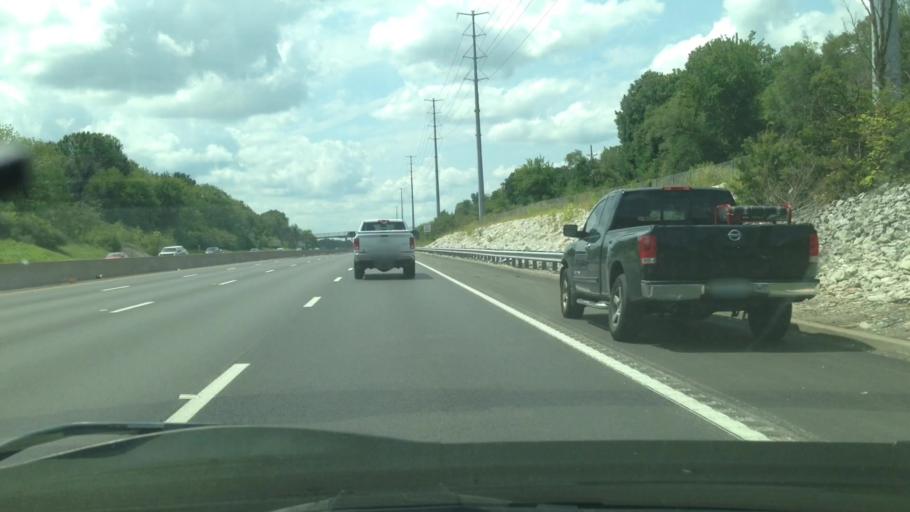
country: US
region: Missouri
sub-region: Saint Louis County
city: Webster Groves
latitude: 38.5785
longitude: -90.3678
